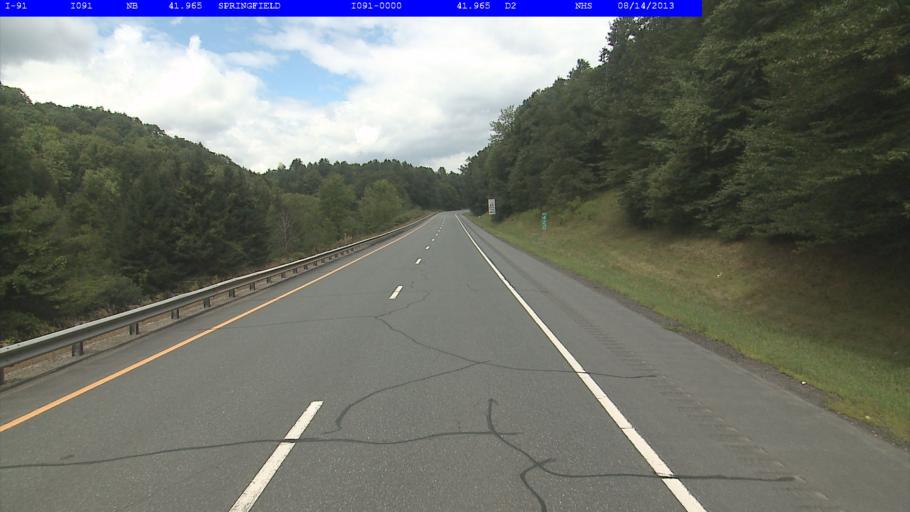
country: US
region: New Hampshire
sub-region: Sullivan County
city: Charlestown
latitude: 43.2707
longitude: -72.4333
